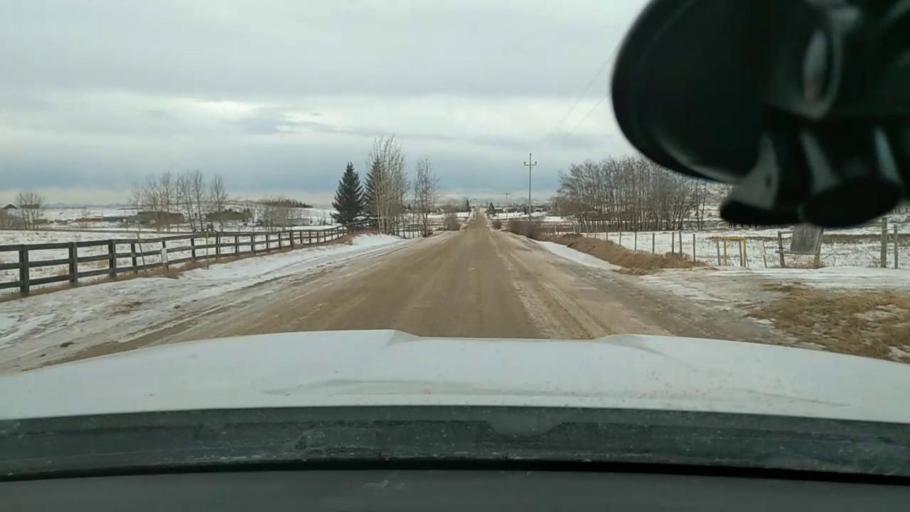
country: CA
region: Alberta
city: Airdrie
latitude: 51.2417
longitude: -113.9233
